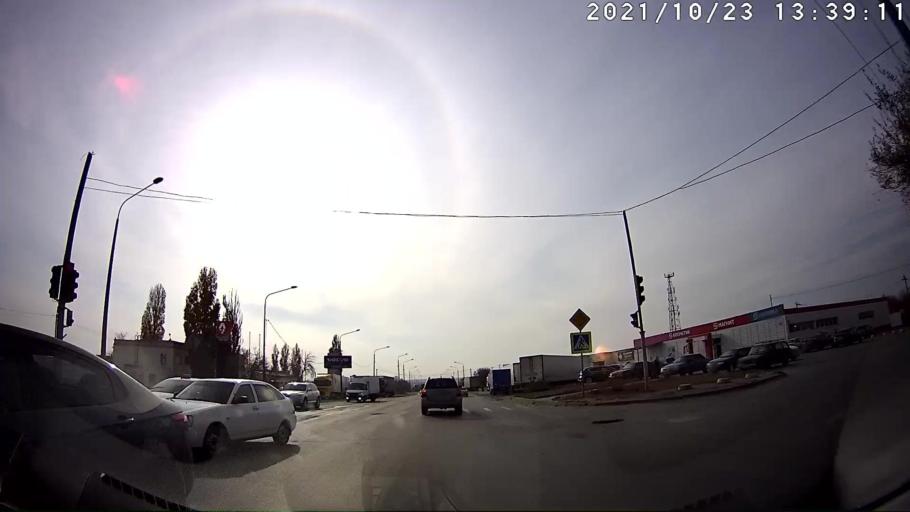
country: RU
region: Volgograd
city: Vodstroy
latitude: 48.8439
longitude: 44.5541
